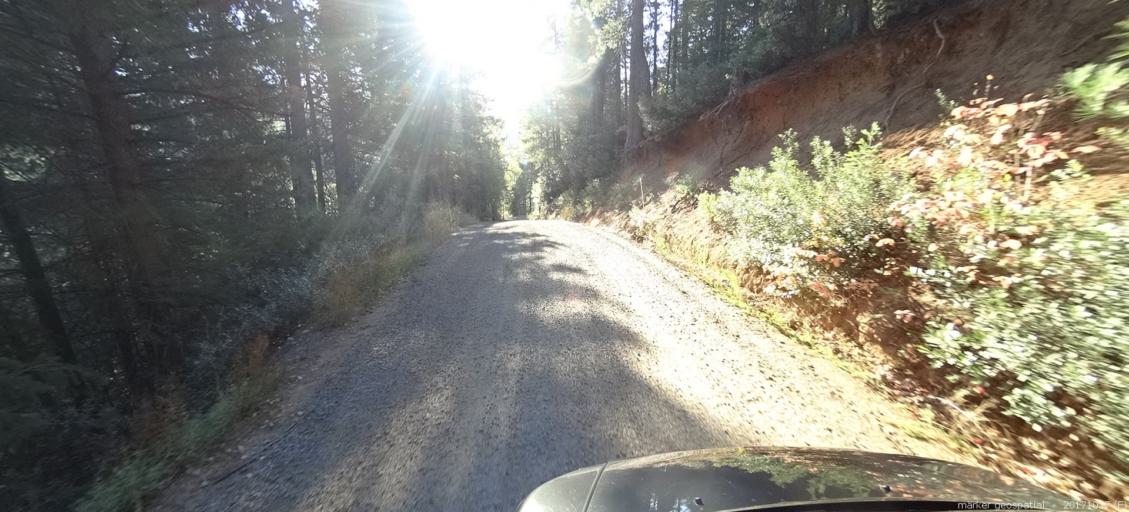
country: US
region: California
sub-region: Shasta County
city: Burney
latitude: 40.9114
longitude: -121.9501
